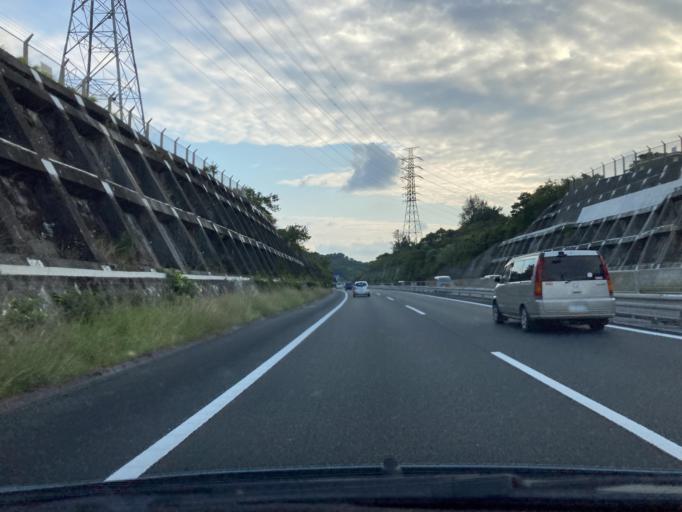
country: JP
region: Okinawa
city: Chatan
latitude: 26.3146
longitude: 127.7884
